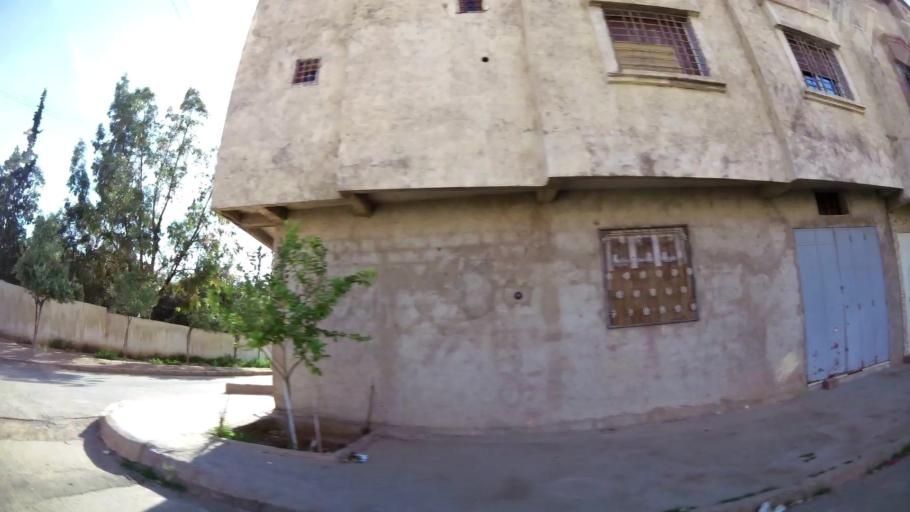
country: MA
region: Oriental
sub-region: Oujda-Angad
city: Oujda
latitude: 34.6686
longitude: -1.8965
